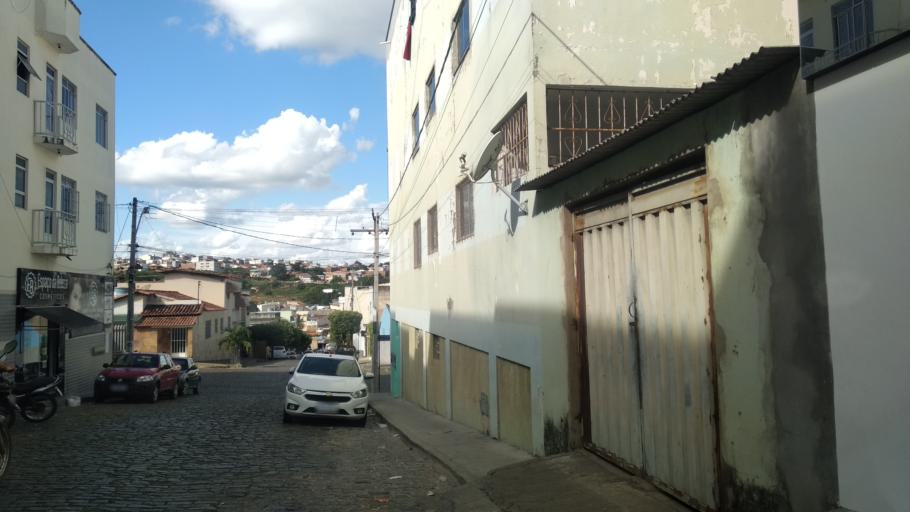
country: BR
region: Bahia
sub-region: Caetite
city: Caetite
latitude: -14.0670
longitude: -42.4922
